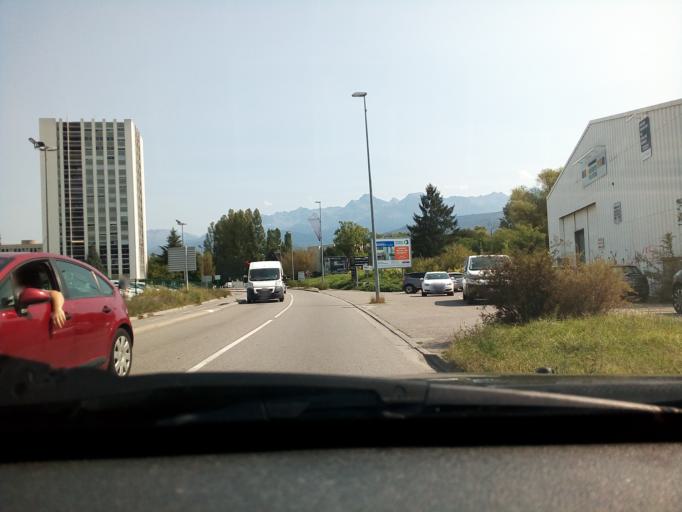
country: FR
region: Rhone-Alpes
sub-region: Departement de l'Isere
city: La Tronche
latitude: 45.1968
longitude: 5.7492
